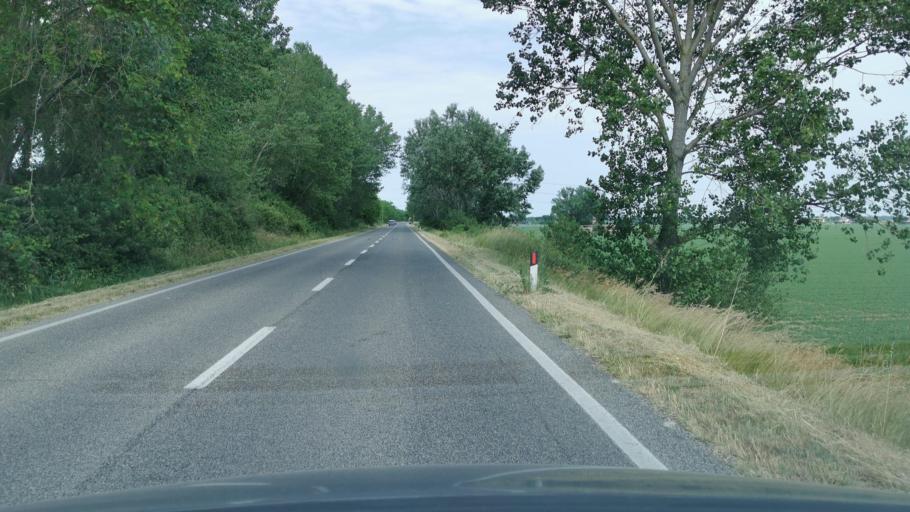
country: IT
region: Emilia-Romagna
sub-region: Provincia di Ravenna
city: Savarna-Conventella
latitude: 44.5231
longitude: 12.1108
